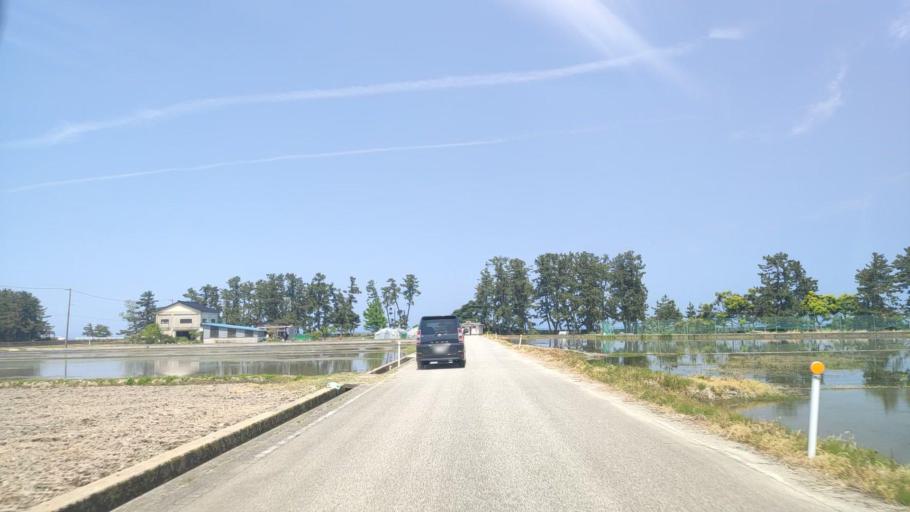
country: JP
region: Toyama
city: Nyuzen
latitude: 36.9613
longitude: 137.5675
